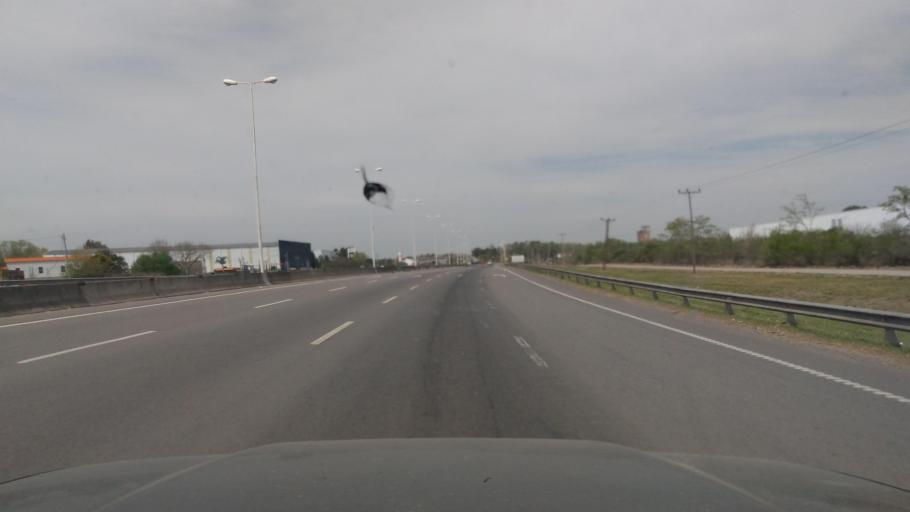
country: AR
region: Buenos Aires
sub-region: Partido de Pilar
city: Pilar
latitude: -34.4135
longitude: -59.0042
